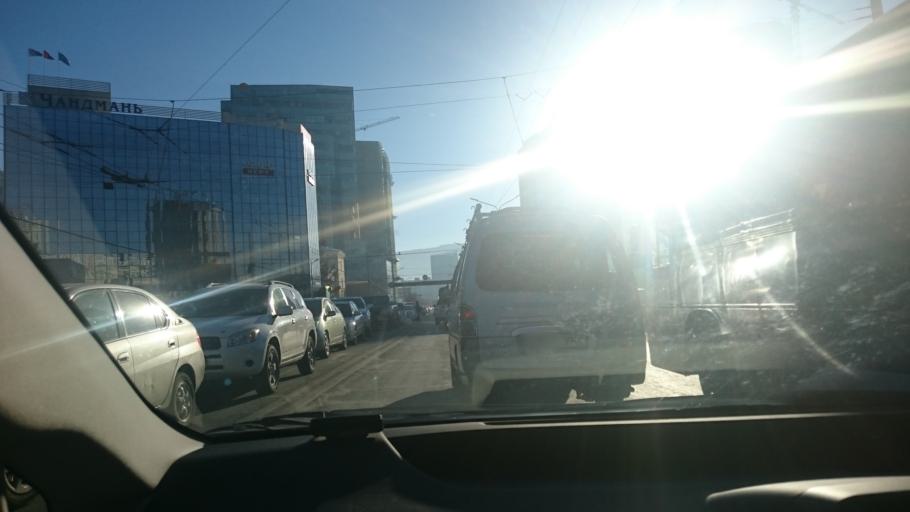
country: MN
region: Ulaanbaatar
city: Ulaanbaatar
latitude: 47.9162
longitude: 106.9160
